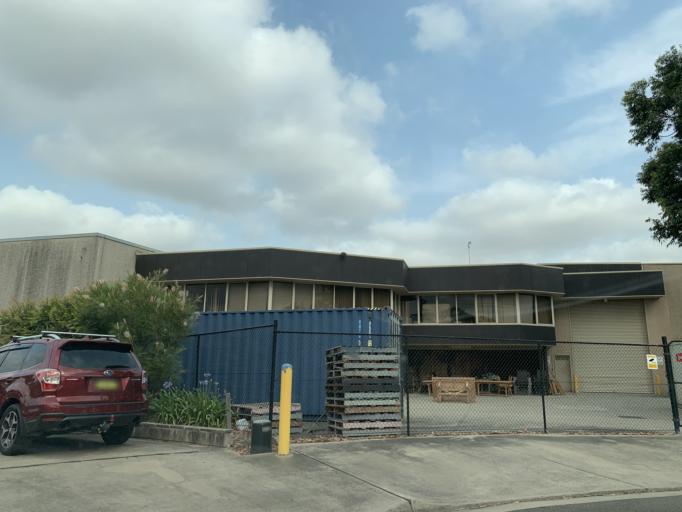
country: AU
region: New South Wales
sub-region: Holroyd
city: Girraween
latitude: -33.7746
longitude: 150.9528
